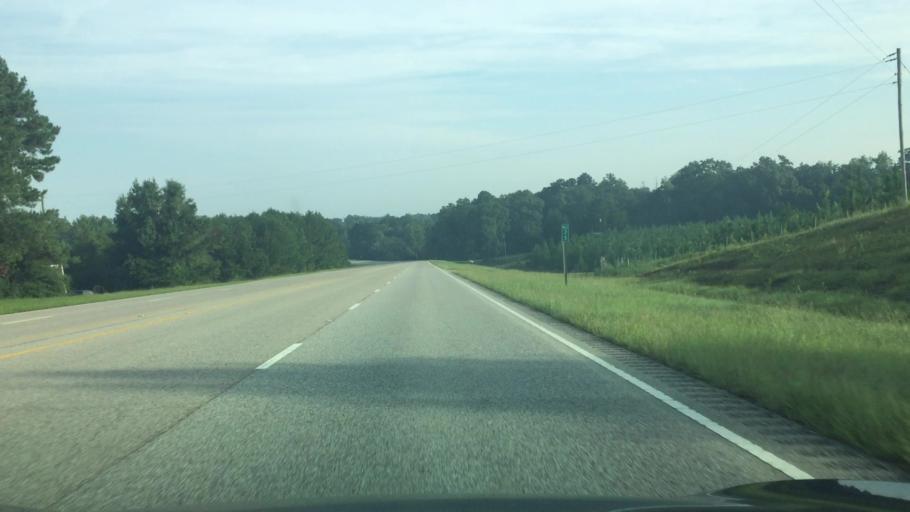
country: US
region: Alabama
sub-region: Covington County
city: Andalusia
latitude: 31.3913
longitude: -86.5723
